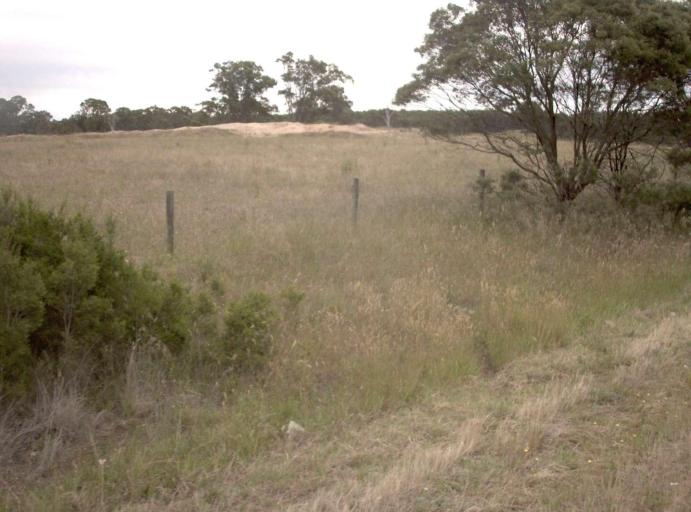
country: AU
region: Victoria
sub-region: East Gippsland
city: Bairnsdale
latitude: -37.9420
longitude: 147.5290
